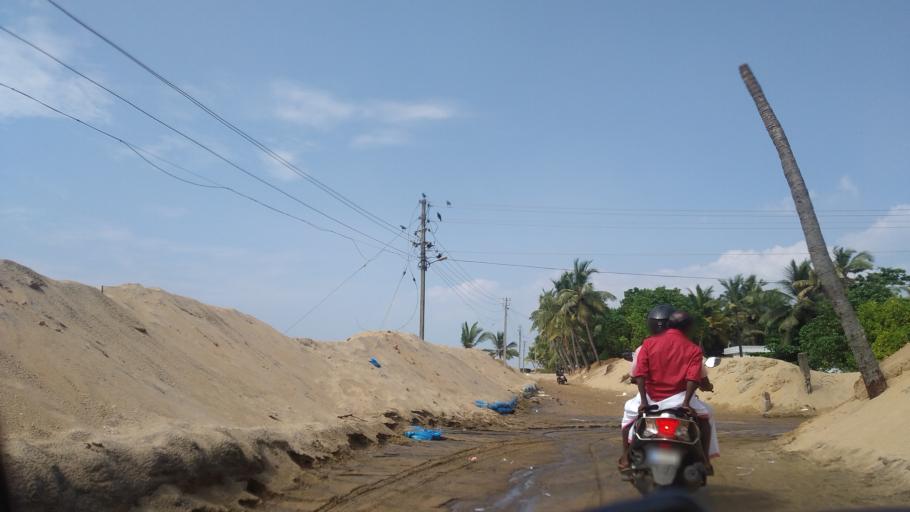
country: IN
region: Kerala
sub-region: Ernakulam
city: Elur
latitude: 10.0739
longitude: 76.1966
